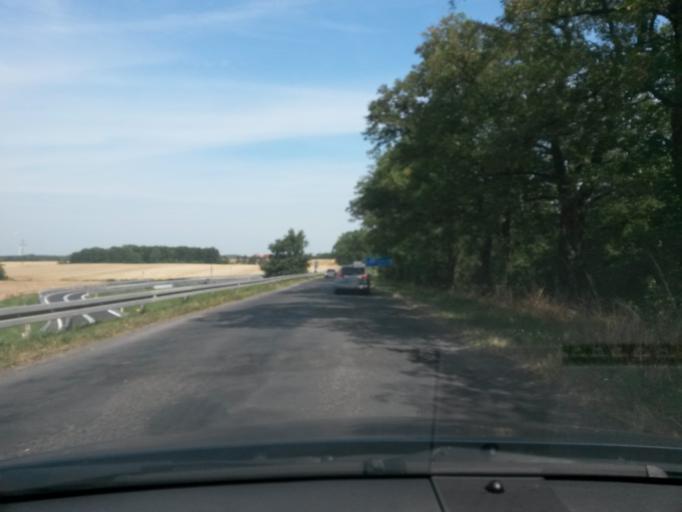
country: PL
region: Lower Silesian Voivodeship
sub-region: Powiat legnicki
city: Legnickie Pole
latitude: 51.1292
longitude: 16.3416
